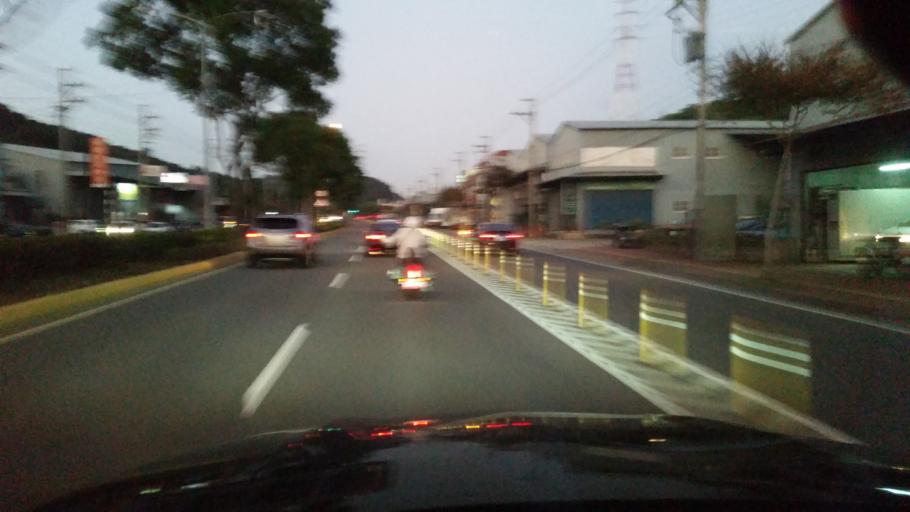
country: TW
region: Taiwan
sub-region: Taoyuan
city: Taoyuan
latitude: 25.0254
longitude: 121.3530
